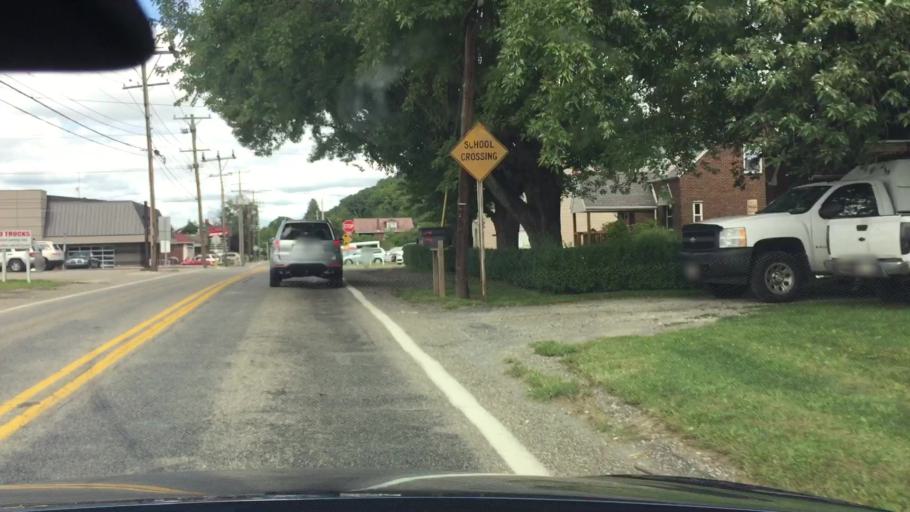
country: US
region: Pennsylvania
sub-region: Allegheny County
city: Cheswick
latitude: 40.5558
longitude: -79.8193
